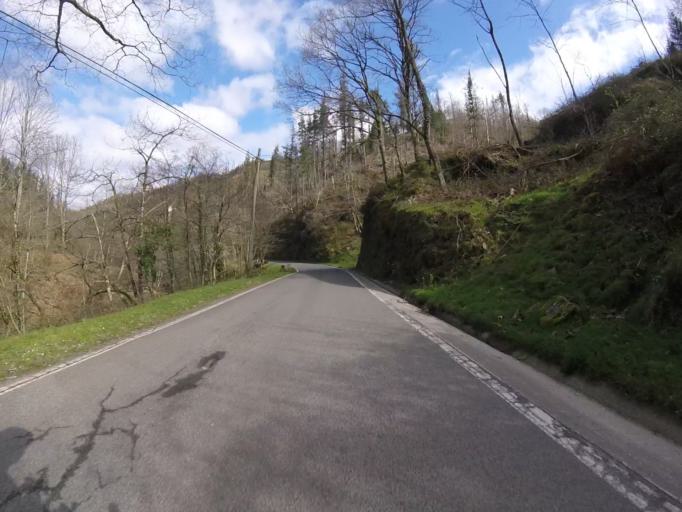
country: ES
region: Navarre
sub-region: Provincia de Navarra
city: Goizueta
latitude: 43.1578
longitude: -1.8495
